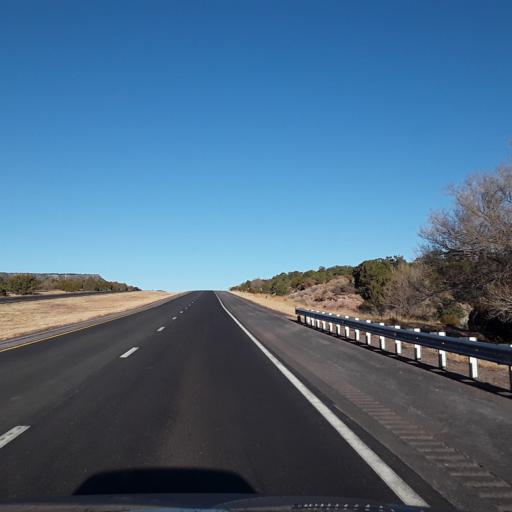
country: US
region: New Mexico
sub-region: San Miguel County
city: Pecos
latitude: 35.4335
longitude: -105.6031
